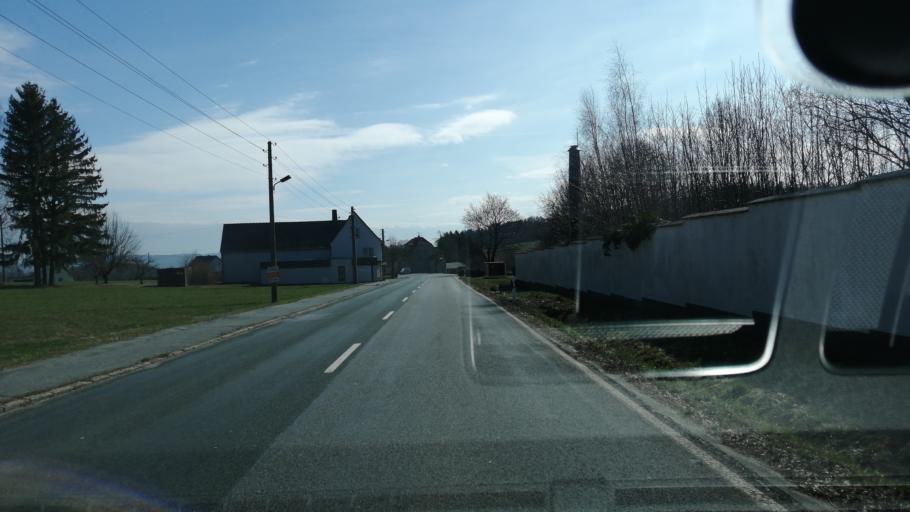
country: DE
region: Saxony
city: Schonbach
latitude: 51.0811
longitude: 14.5777
